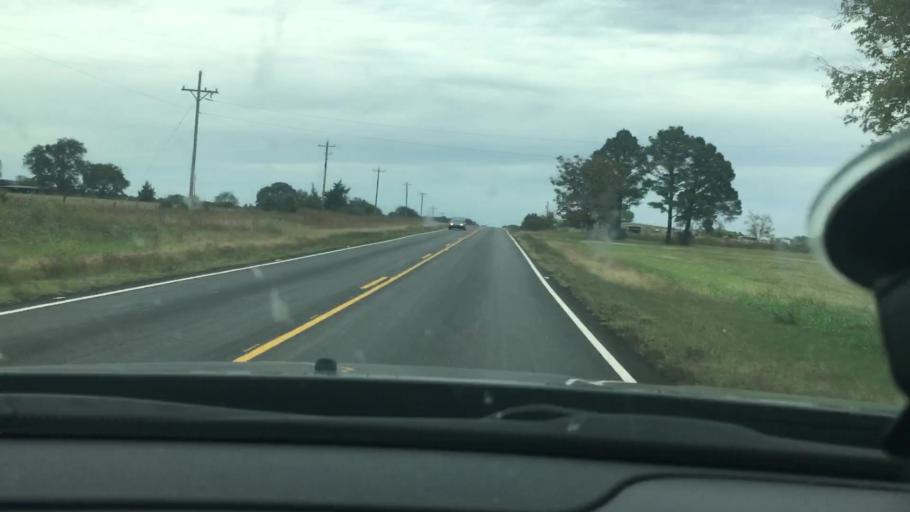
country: US
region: Oklahoma
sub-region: Coal County
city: Coalgate
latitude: 34.3952
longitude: -96.4245
